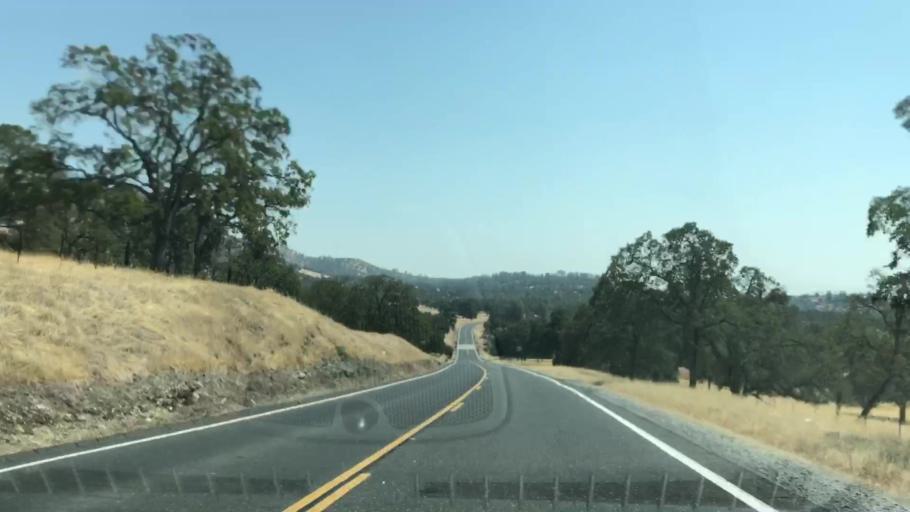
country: US
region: California
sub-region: Calaveras County
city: Copperopolis
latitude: 37.9637
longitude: -120.6181
